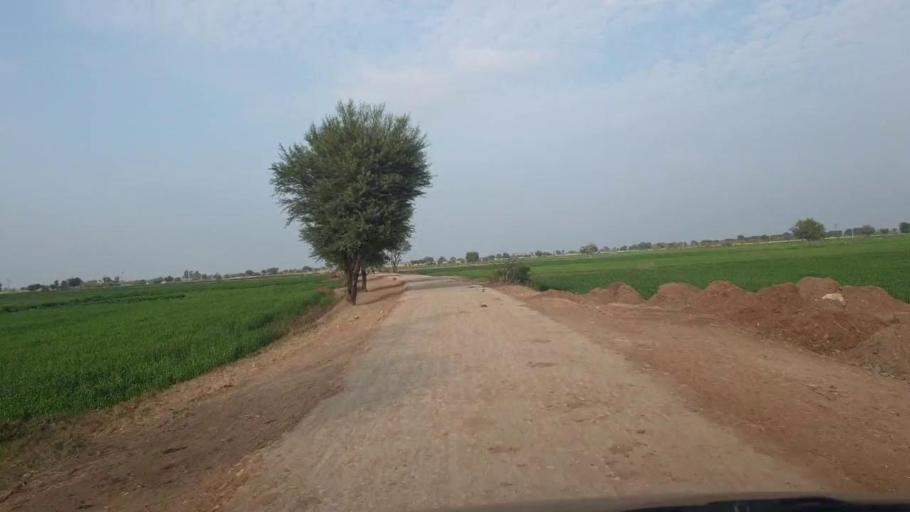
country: PK
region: Sindh
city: Shahdadpur
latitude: 25.8871
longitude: 68.7258
